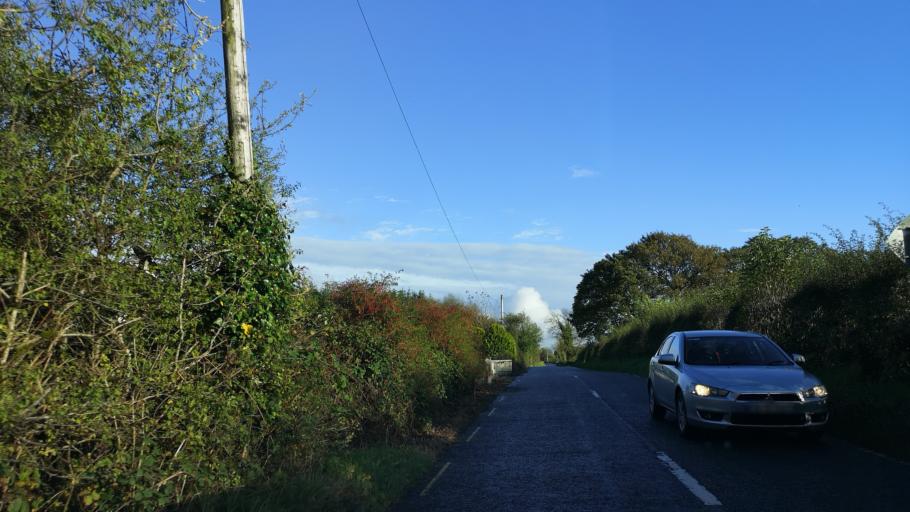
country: IE
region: Connaught
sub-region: Roscommon
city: Castlerea
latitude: 53.8002
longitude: -8.5000
